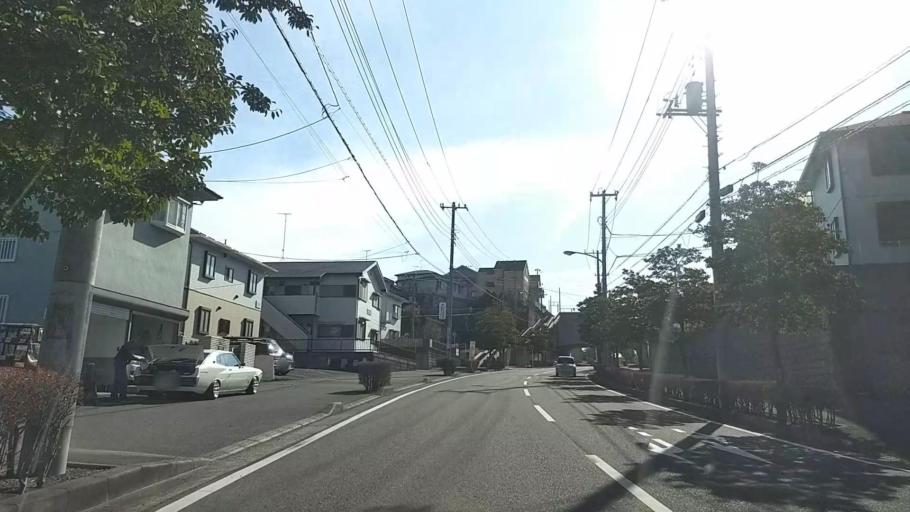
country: JP
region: Kanagawa
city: Hadano
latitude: 35.3666
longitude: 139.2261
